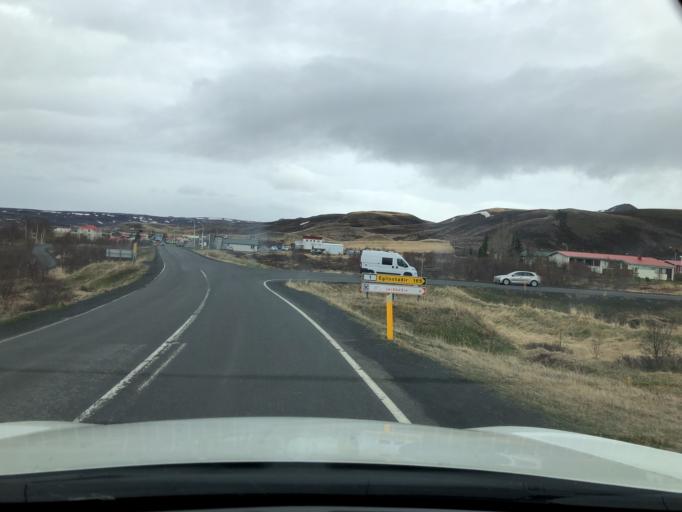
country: IS
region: Northeast
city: Laugar
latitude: 65.6392
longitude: -16.9105
